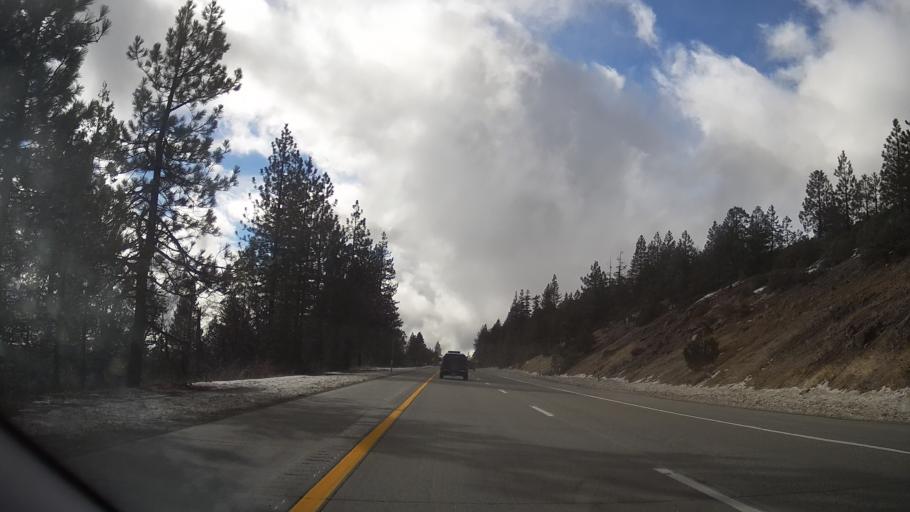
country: US
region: California
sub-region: Sierra County
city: Downieville
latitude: 39.3147
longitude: -120.6264
